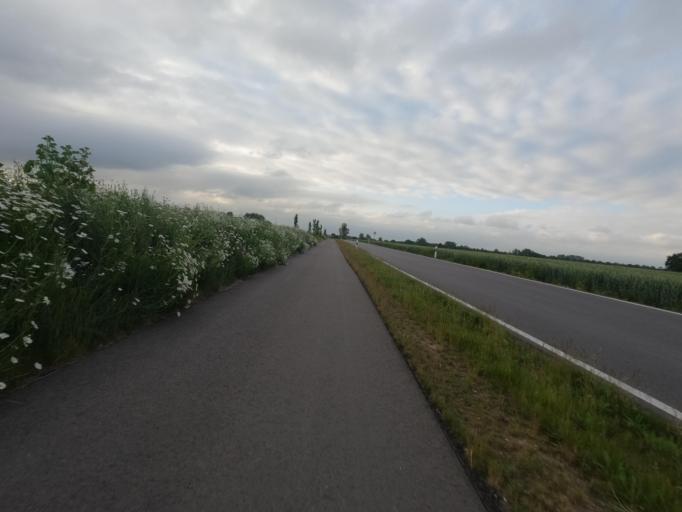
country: NL
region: Limburg
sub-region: Gemeente Roerdalen
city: Vlodrop
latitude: 51.1159
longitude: 6.1099
